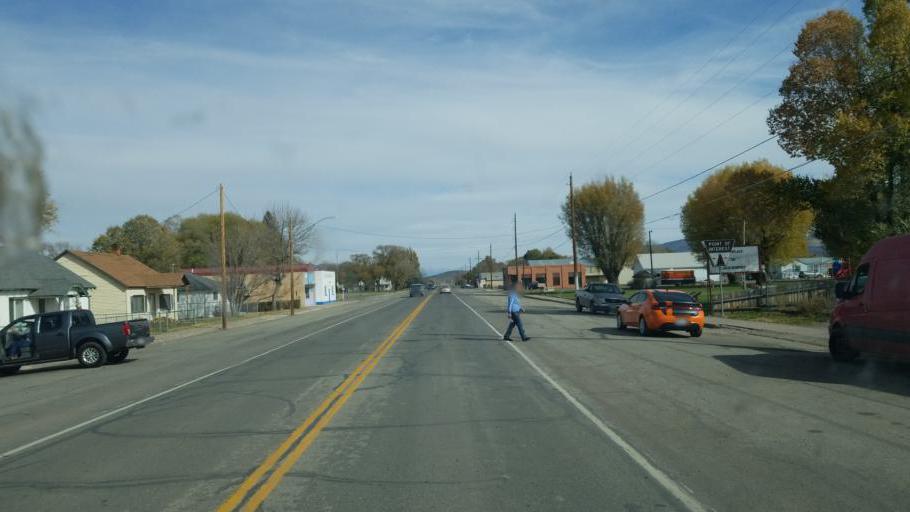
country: US
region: Colorado
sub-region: Conejos County
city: Conejos
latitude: 37.1739
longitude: -105.9366
